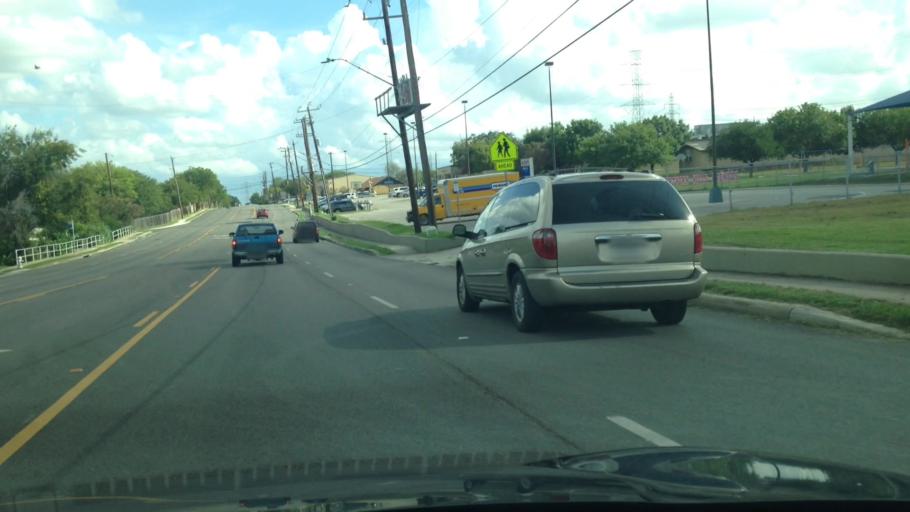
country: US
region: Texas
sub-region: Bexar County
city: Windcrest
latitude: 29.5697
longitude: -98.3956
